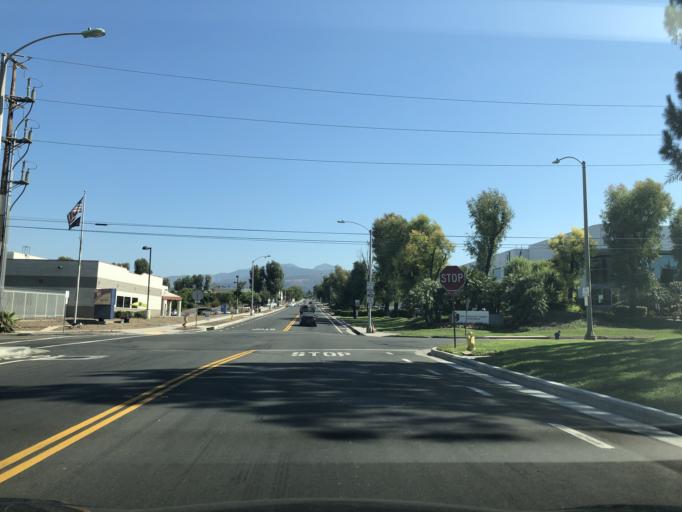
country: US
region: California
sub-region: Riverside County
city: El Cerrito
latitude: 33.8542
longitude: -117.5391
